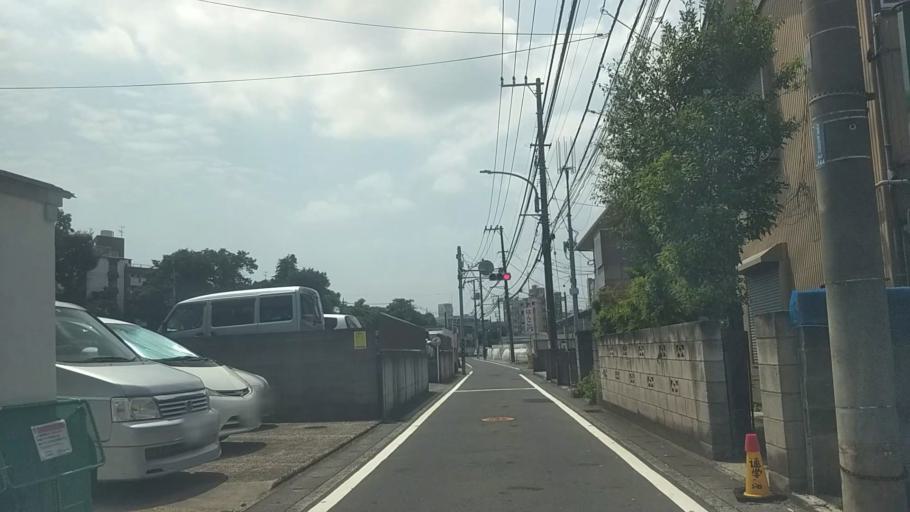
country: JP
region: Kanagawa
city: Yokohama
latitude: 35.5087
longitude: 139.6200
